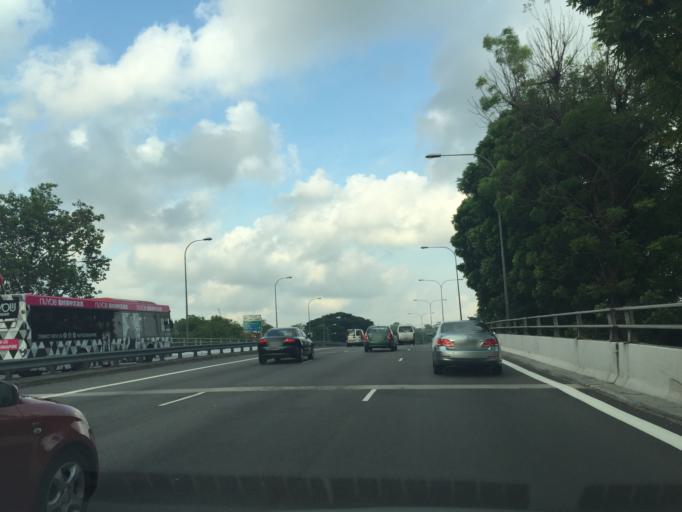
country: SG
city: Singapore
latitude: 1.3292
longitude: 103.8413
